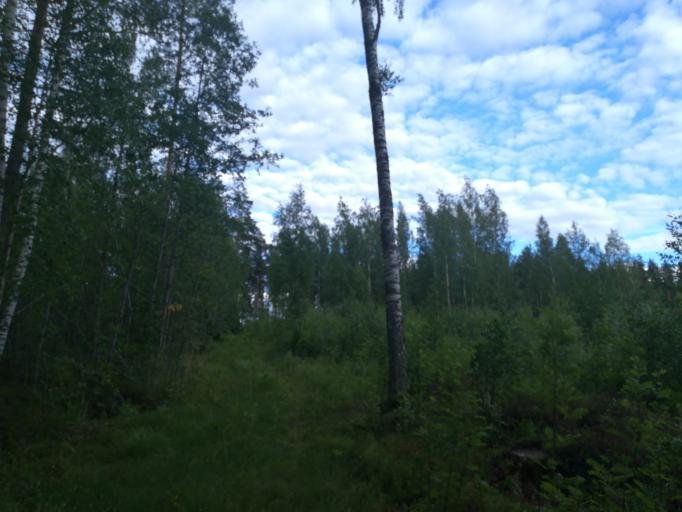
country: FI
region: South Karelia
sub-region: Lappeenranta
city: Savitaipale
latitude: 61.5031
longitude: 27.8357
